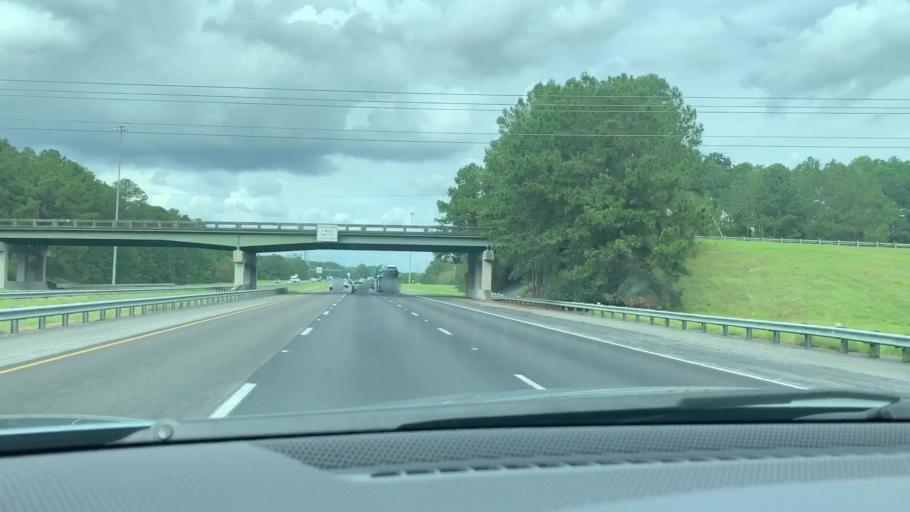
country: US
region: Georgia
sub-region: Liberty County
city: Midway
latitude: 31.7774
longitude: -81.3788
